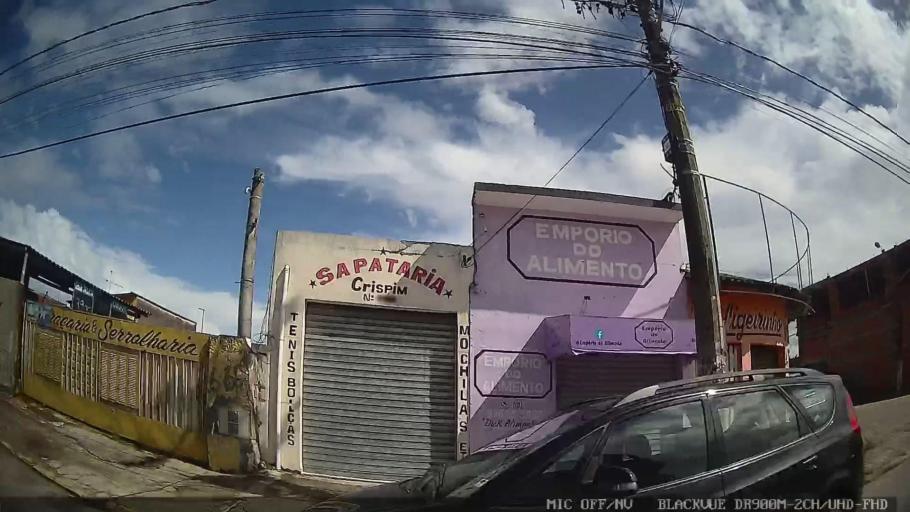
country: BR
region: Sao Paulo
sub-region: Itanhaem
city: Itanhaem
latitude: -24.2402
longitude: -46.8948
